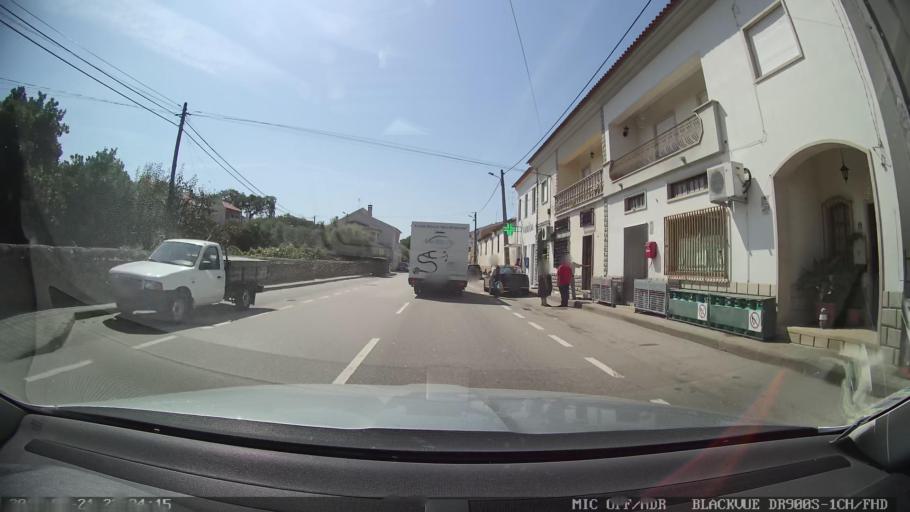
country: PT
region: Guarda
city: Alcains
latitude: 39.8826
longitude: -7.3969
